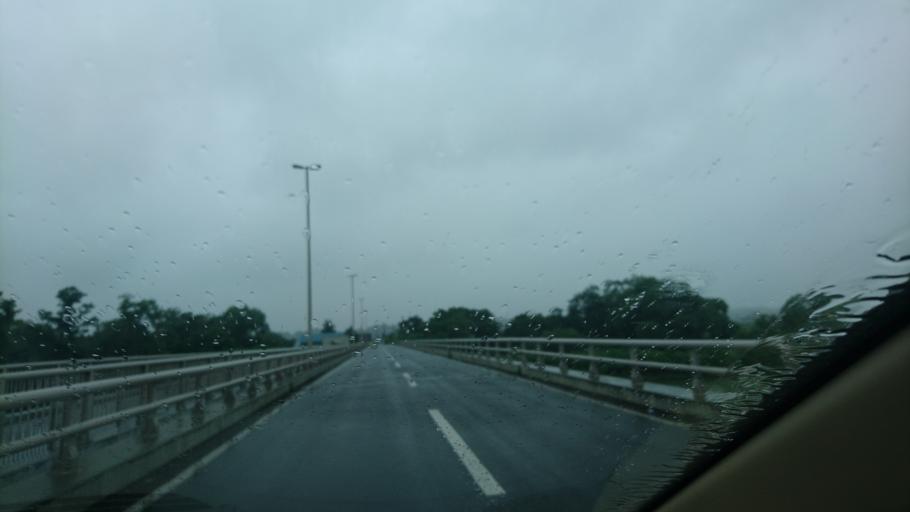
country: JP
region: Iwate
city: Kitakami
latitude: 39.2770
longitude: 141.1131
